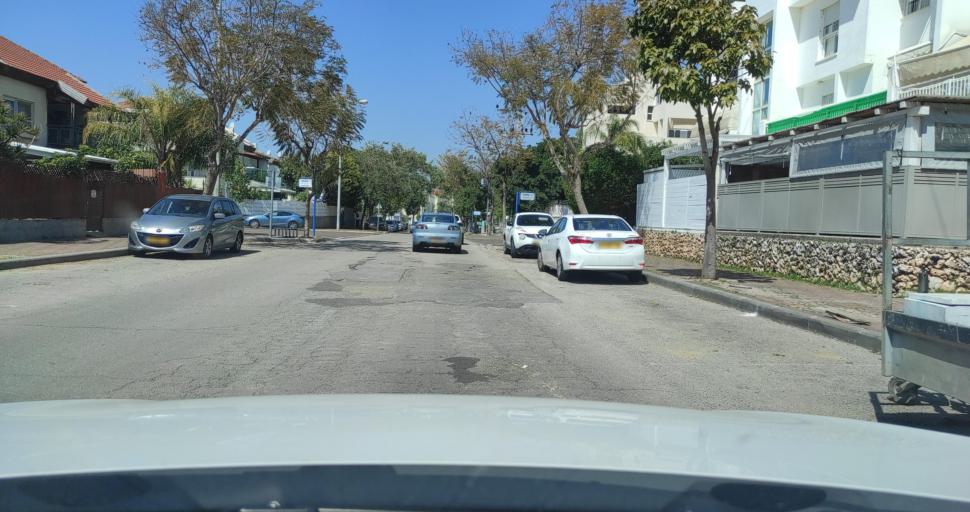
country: IL
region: Central District
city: Nordiyya
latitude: 32.3050
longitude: 34.8827
